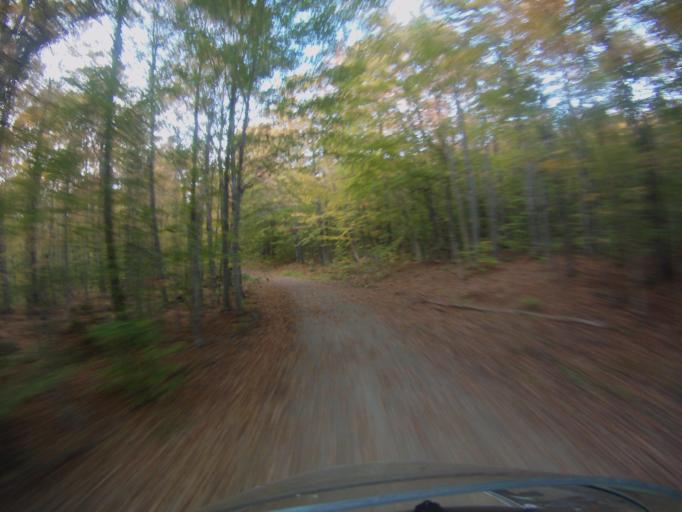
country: US
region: Vermont
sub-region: Addison County
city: Bristol
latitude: 44.0950
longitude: -72.9514
